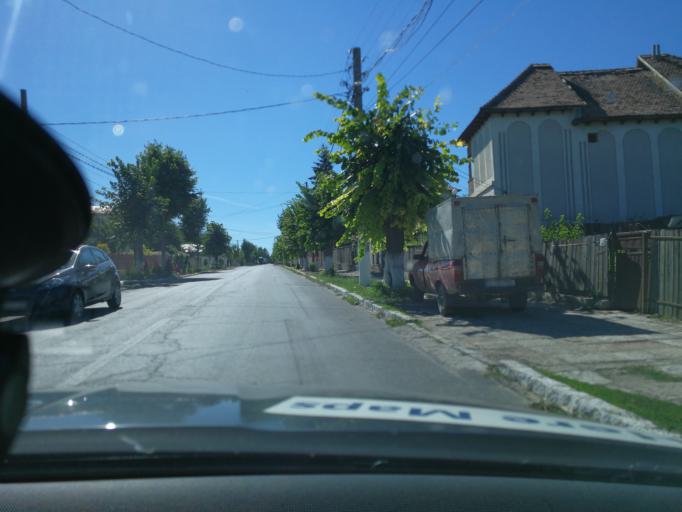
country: RO
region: Tulcea
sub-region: Oras Macin
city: Macin
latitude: 45.2426
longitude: 28.1442
